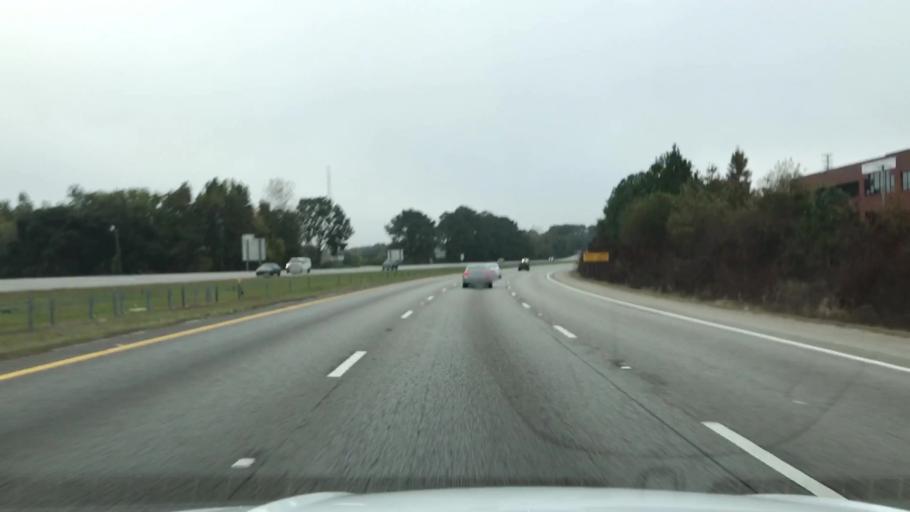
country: US
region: South Carolina
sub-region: Charleston County
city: North Charleston
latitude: 32.8473
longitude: -80.0180
